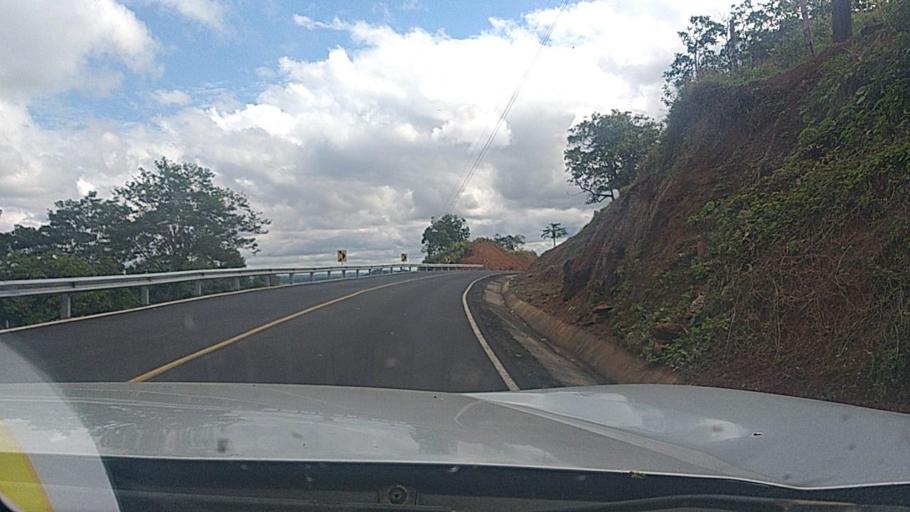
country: NI
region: Atlantico Sur
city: Muelle de los Bueyes
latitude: 12.1292
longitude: -84.4358
